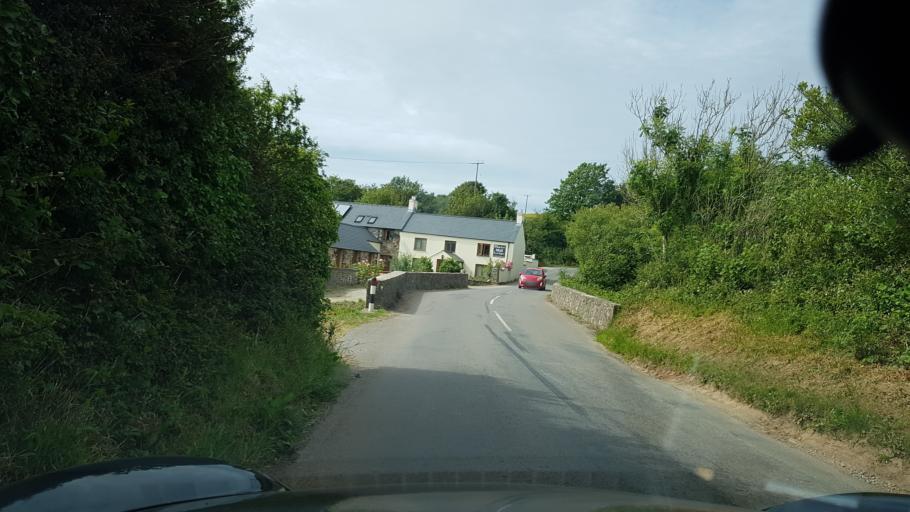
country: GB
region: Wales
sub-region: Pembrokeshire
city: Dale
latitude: 51.7381
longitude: -5.1564
